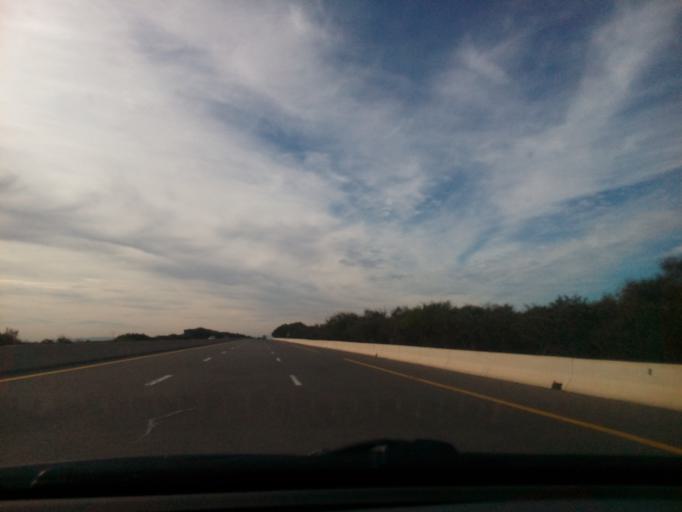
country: DZ
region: Sidi Bel Abbes
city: Sidi Bel Abbes
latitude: 35.2049
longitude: -0.6891
